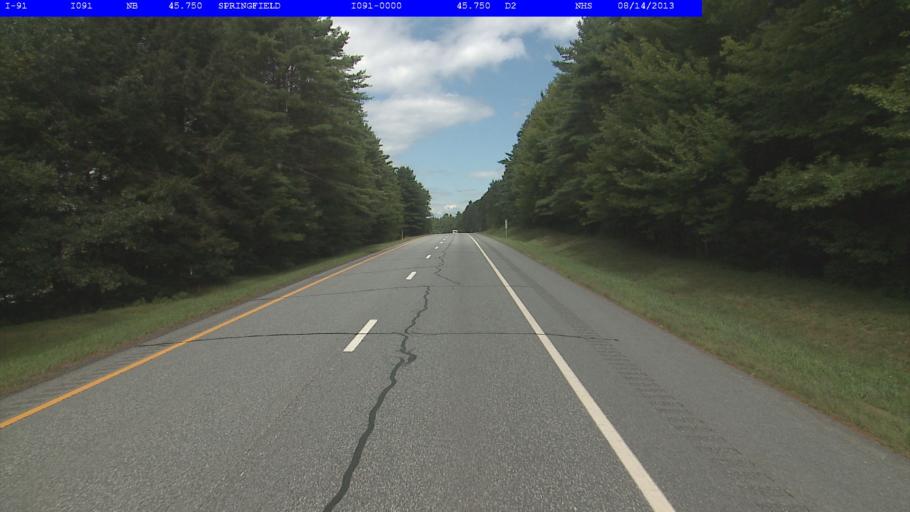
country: US
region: Vermont
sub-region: Windsor County
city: Springfield
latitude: 43.3234
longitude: -72.4195
